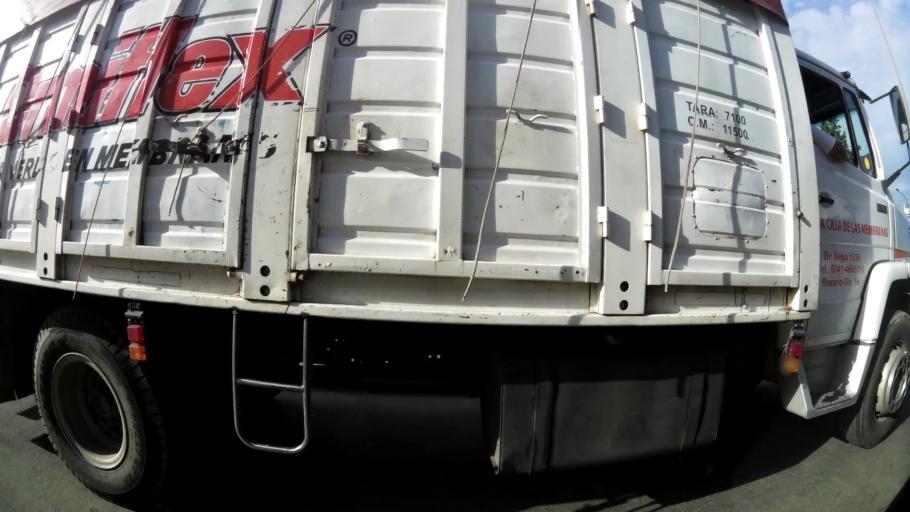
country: AR
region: Santa Fe
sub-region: Departamento de Rosario
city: Rosario
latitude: -32.9741
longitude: -60.6744
